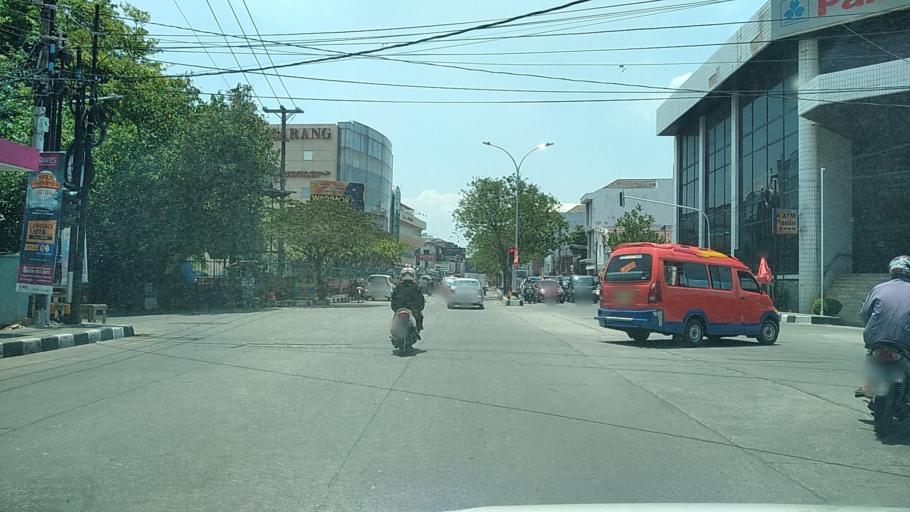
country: ID
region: Central Java
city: Semarang
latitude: -6.9708
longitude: 110.4281
